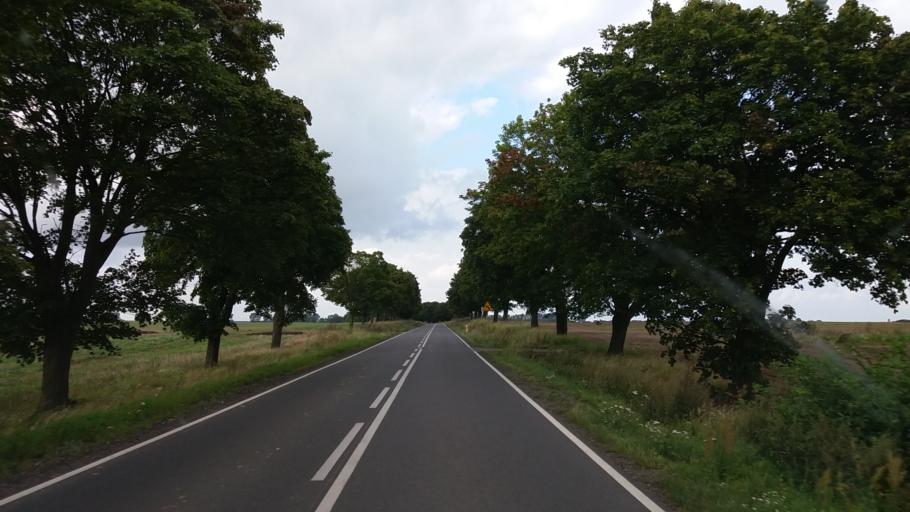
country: PL
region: West Pomeranian Voivodeship
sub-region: Powiat choszczenski
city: Choszczno
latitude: 53.1376
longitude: 15.3791
